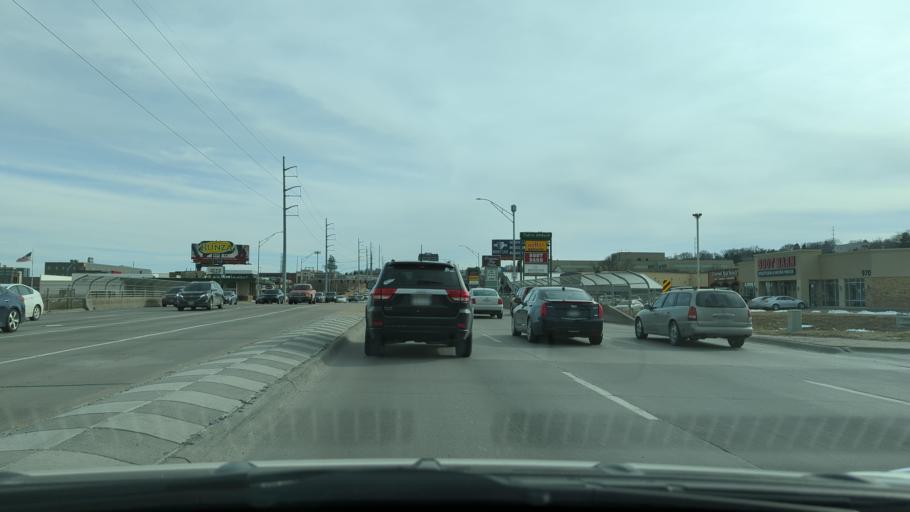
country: US
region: Nebraska
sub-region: Douglas County
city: Ralston
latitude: 41.2511
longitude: -96.0240
